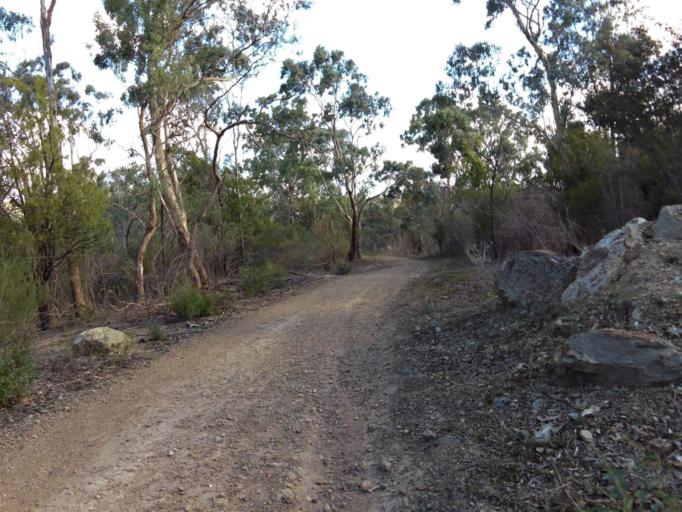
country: AU
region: Victoria
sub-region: Nillumbik
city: North Warrandyte
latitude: -37.7378
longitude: 145.2012
